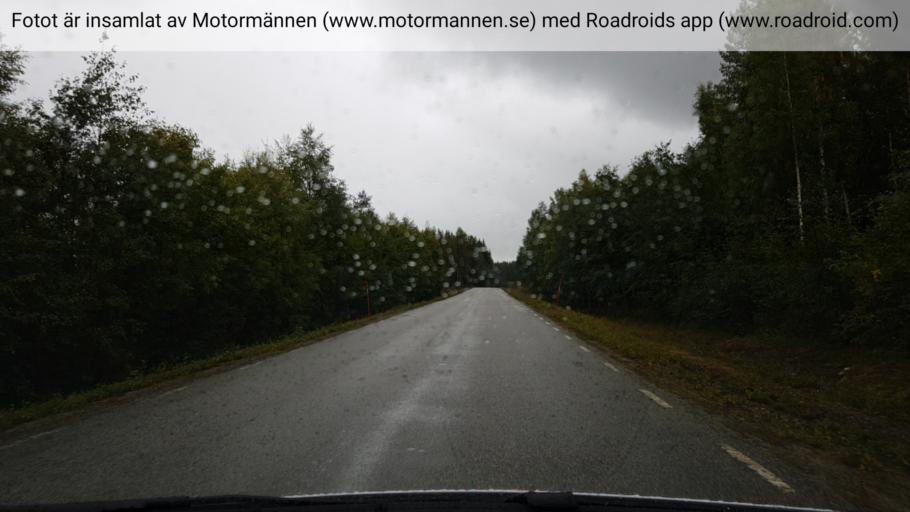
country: SE
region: Vaesterbotten
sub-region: Vannas Kommun
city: Vannasby
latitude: 64.0085
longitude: 19.9222
